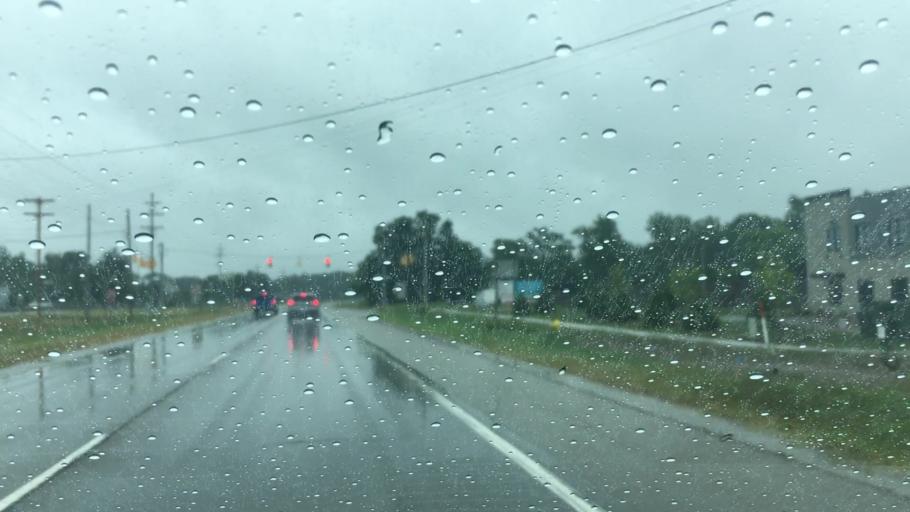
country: US
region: Michigan
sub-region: Ottawa County
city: Jenison
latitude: 42.8892
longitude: -85.8277
